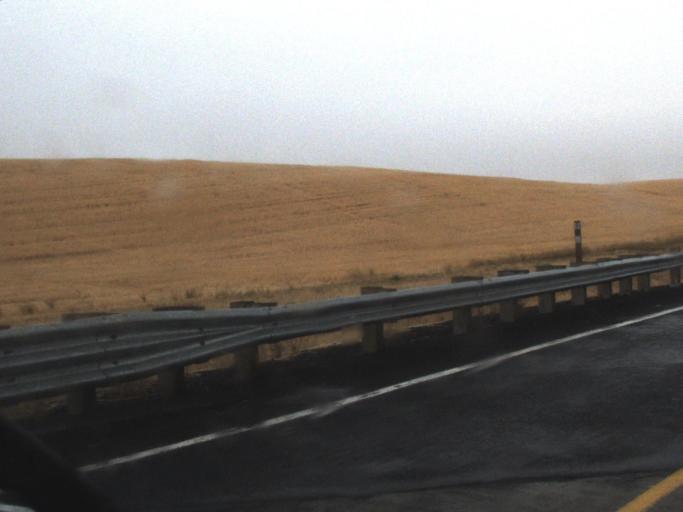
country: US
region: Washington
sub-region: Lincoln County
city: Davenport
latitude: 47.4458
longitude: -118.1859
